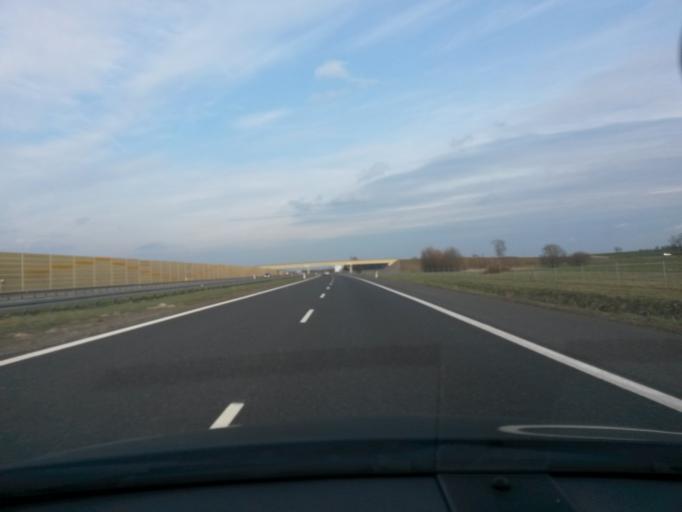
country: PL
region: Lodz Voivodeship
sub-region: Powiat zgierski
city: Parzeczew
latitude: 51.9401
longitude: 19.2019
